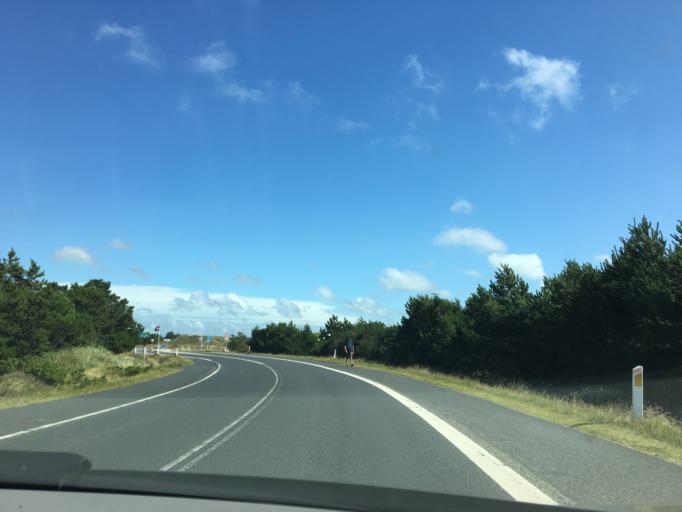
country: DK
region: South Denmark
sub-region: Varde Kommune
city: Oksbol
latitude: 55.7354
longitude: 8.1858
